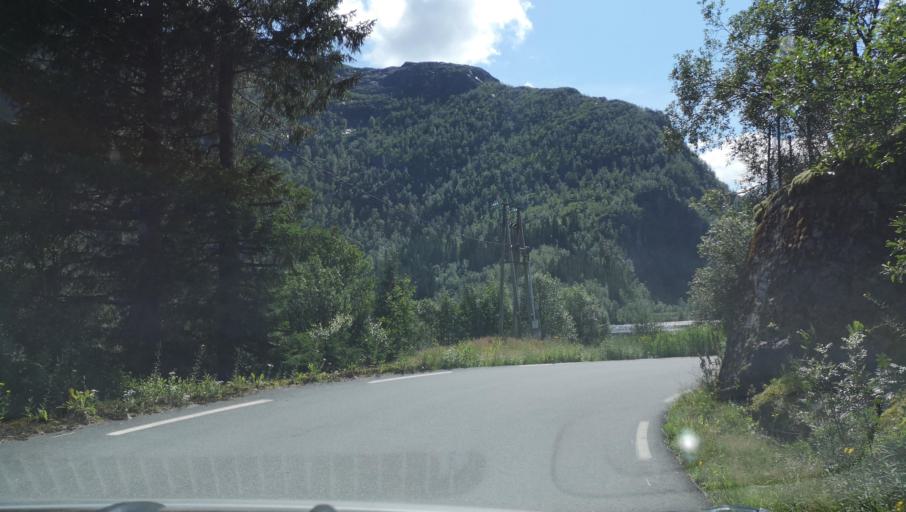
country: NO
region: Hordaland
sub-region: Modalen
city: Mo
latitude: 60.7861
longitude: 5.9652
